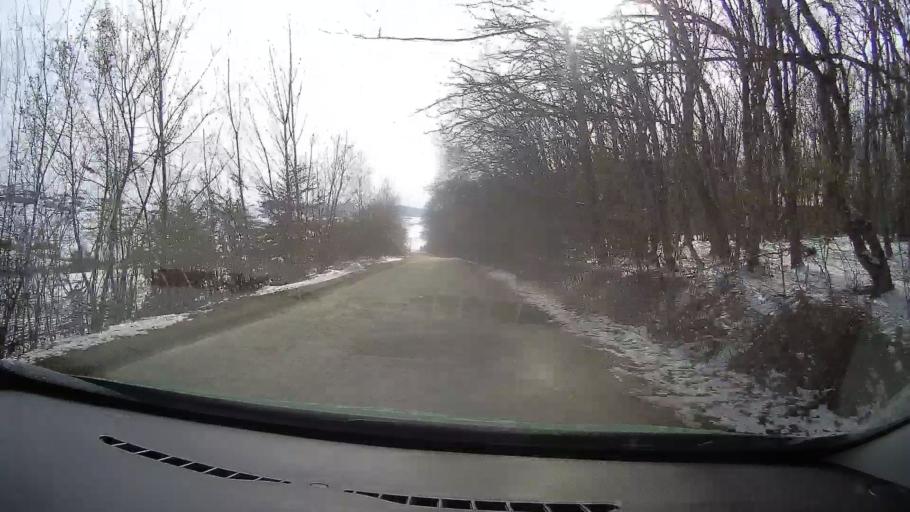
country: RO
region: Sibiu
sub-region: Comuna Bradeni
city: Bradeni
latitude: 46.0989
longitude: 24.8370
